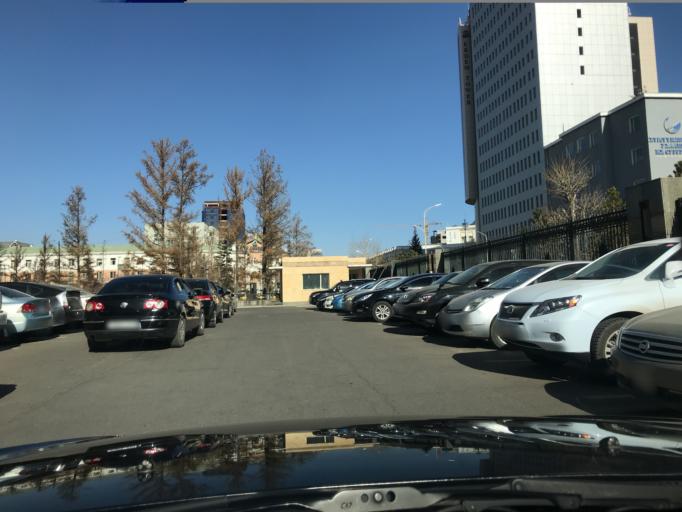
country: MN
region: Ulaanbaatar
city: Ulaanbaatar
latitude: 47.9210
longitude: 106.9184
